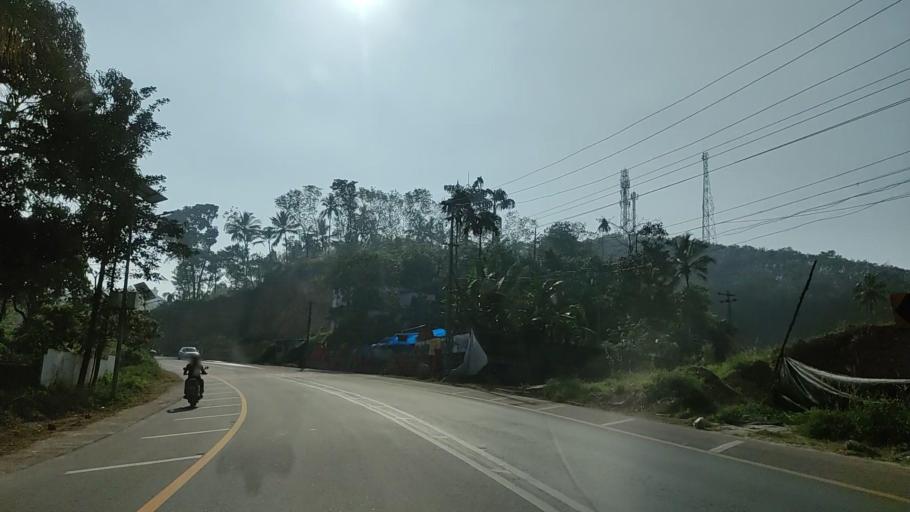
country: IN
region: Kerala
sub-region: Kollam
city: Punalur
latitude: 8.9674
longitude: 76.8319
